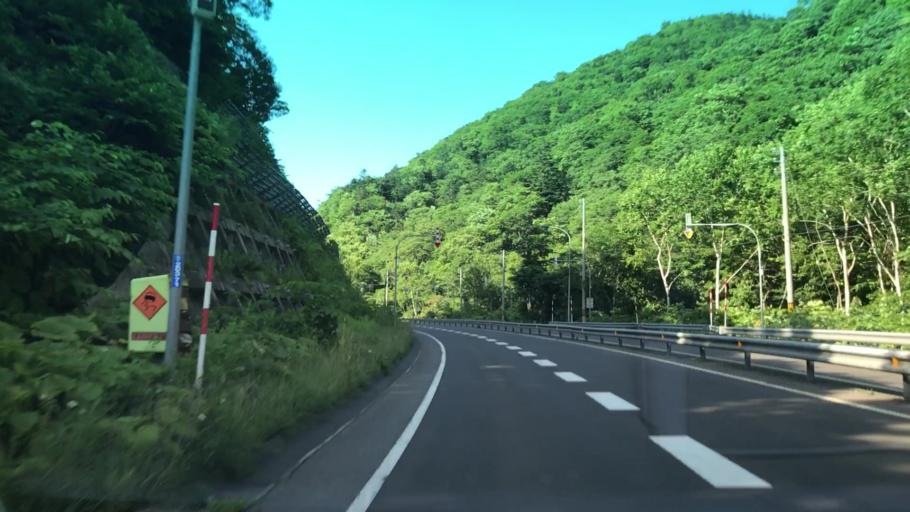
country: JP
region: Hokkaido
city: Yoichi
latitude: 43.0432
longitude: 140.6810
